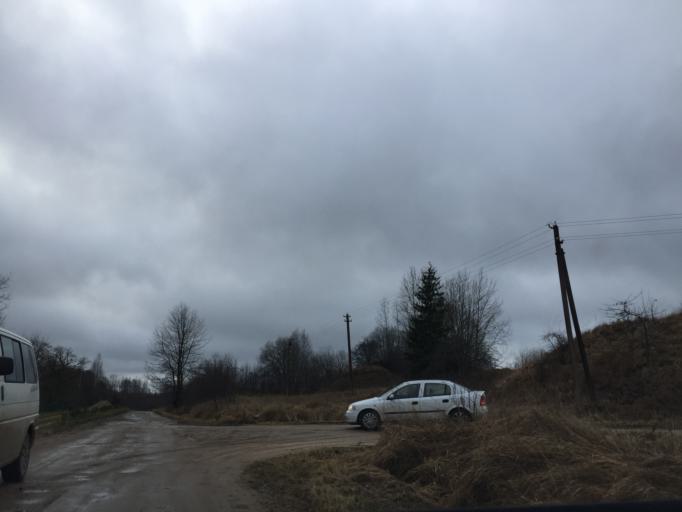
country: LV
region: Broceni
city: Broceni
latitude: 56.6672
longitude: 22.5534
